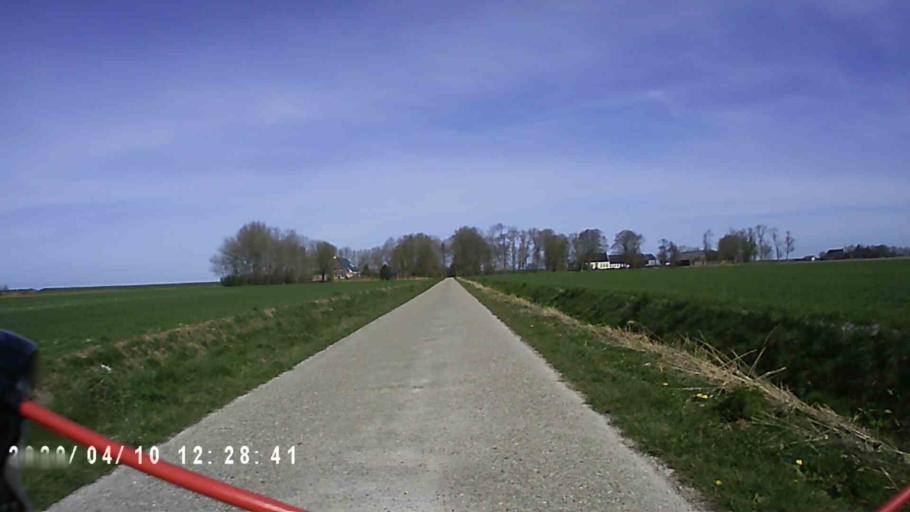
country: NL
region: Groningen
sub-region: Gemeente De Marne
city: Ulrum
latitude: 53.3996
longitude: 6.4098
